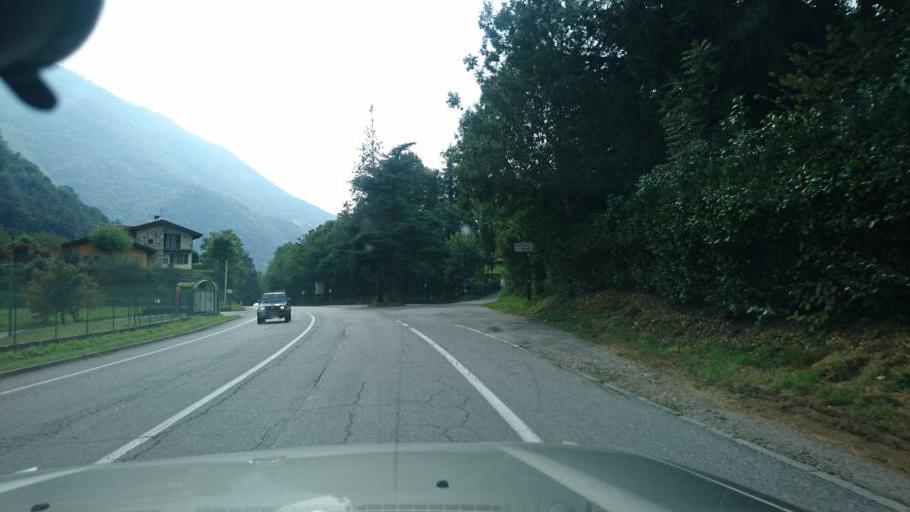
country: IT
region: Lombardy
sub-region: Provincia di Brescia
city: Vestone
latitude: 45.7151
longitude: 10.4133
